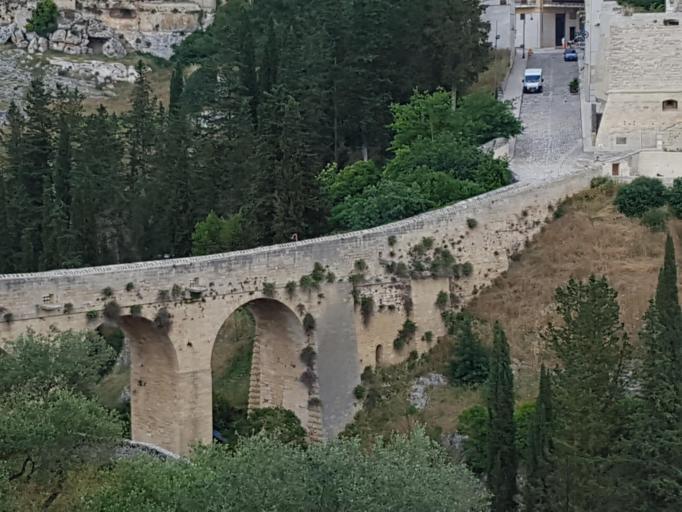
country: IT
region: Apulia
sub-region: Provincia di Bari
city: Gravina in Puglia
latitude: 40.8192
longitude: 16.4119
